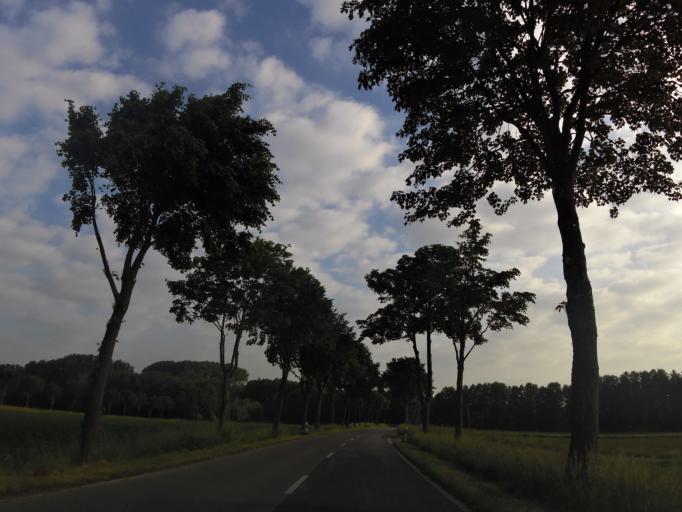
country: DE
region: North Rhine-Westphalia
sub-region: Regierungsbezirk Koln
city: Selfkant
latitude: 50.9895
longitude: 5.9422
